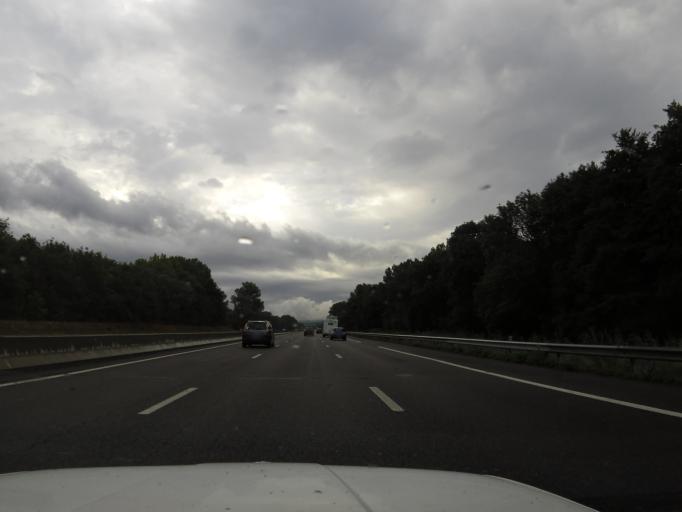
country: FR
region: Rhone-Alpes
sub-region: Departement de l'Isere
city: La Verpilliere
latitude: 45.6398
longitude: 5.1484
